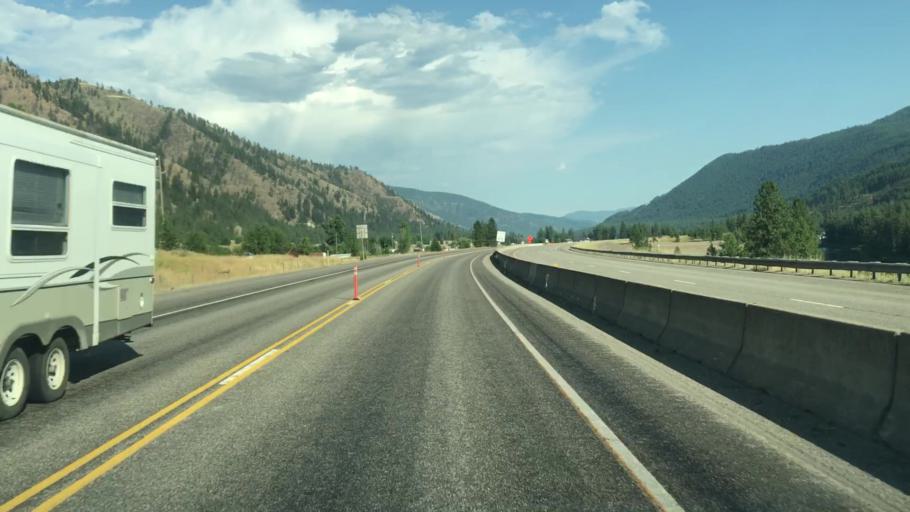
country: US
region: Montana
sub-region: Mineral County
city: Superior
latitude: 47.2153
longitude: -114.9461
